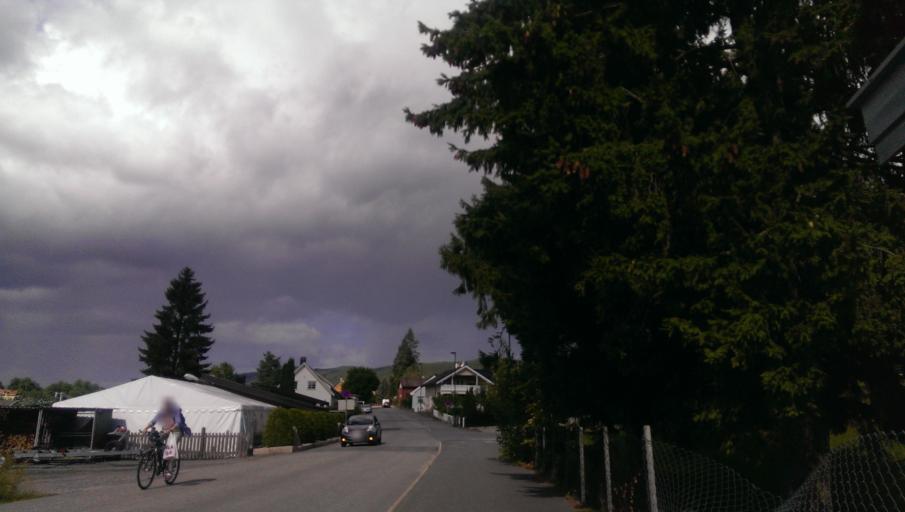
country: NO
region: Buskerud
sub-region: Kongsberg
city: Kongsberg
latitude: 59.6587
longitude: 9.6536
